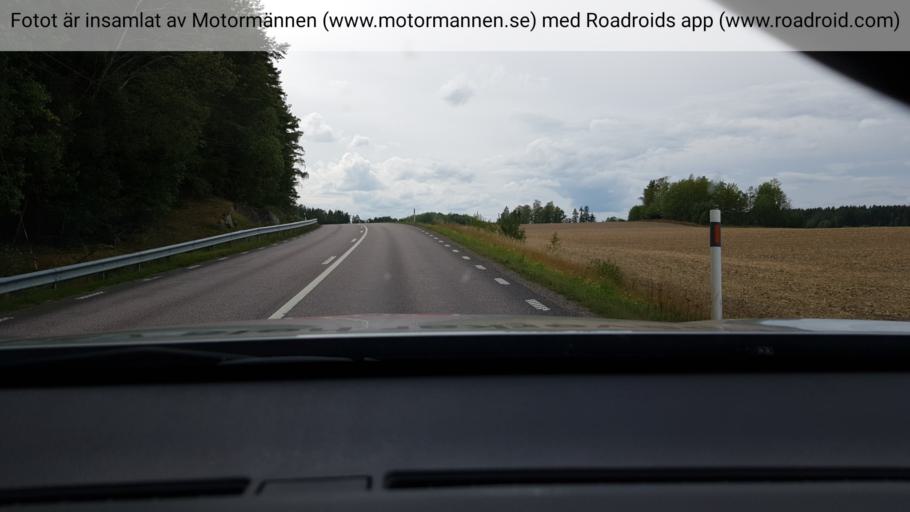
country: SE
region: Soedermanland
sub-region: Gnesta Kommun
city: Gnesta
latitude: 59.0551
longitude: 17.2169
